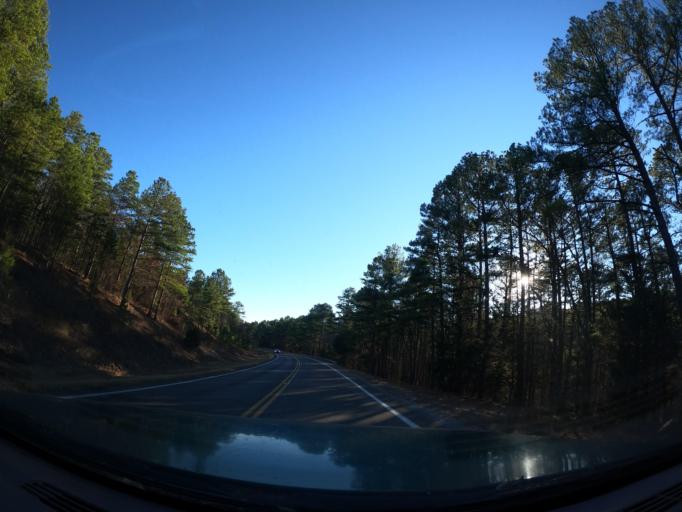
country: US
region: Oklahoma
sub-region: Latimer County
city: Wilburton
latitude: 34.9674
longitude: -95.3575
